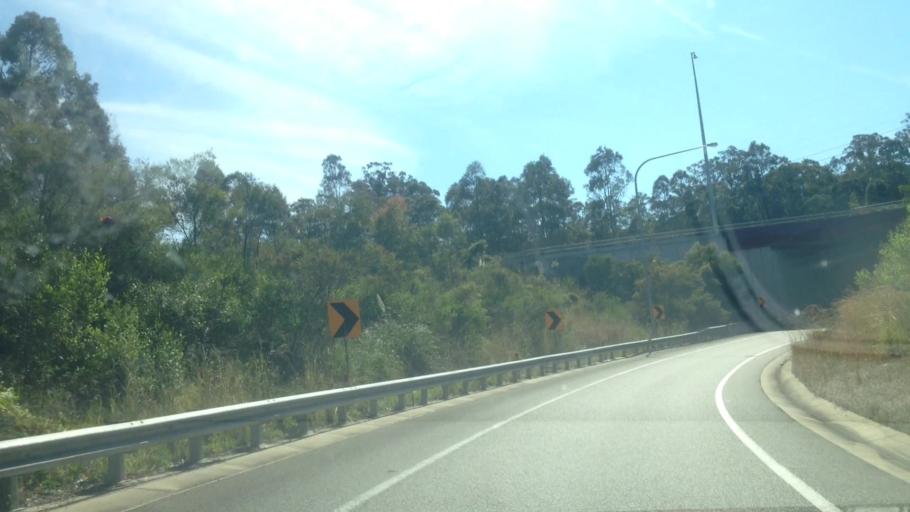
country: AU
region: New South Wales
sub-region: Lake Macquarie Shire
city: Holmesville
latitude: -32.8886
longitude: 151.5983
